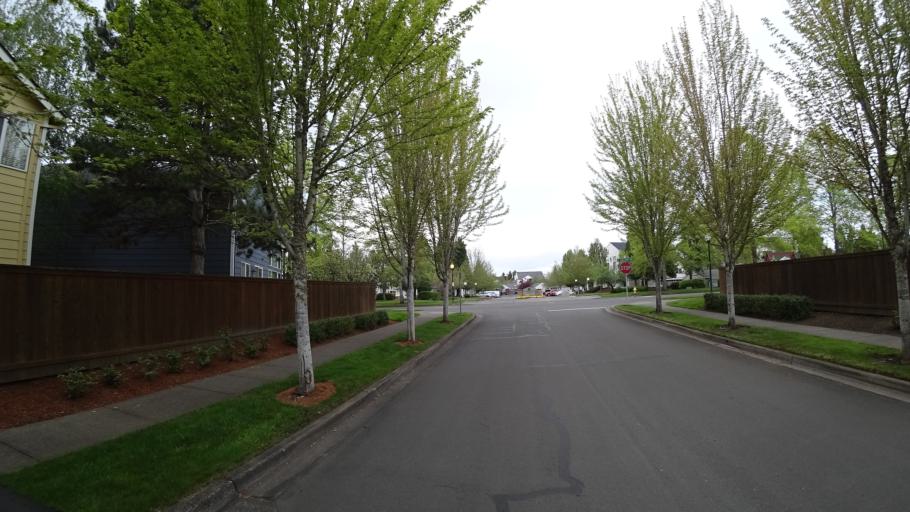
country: US
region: Oregon
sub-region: Washington County
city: Hillsboro
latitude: 45.5420
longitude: -122.9683
